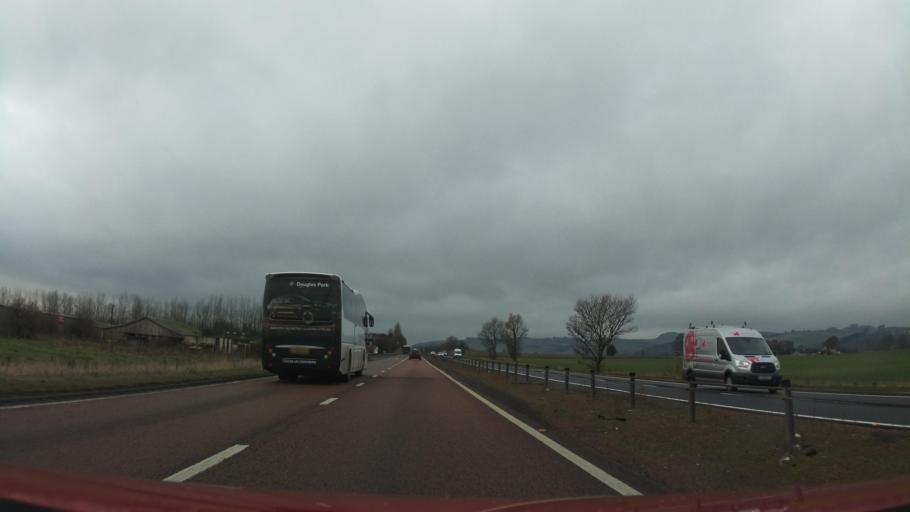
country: GB
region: Scotland
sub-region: Perth and Kinross
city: Errol
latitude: 56.4308
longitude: -3.2059
